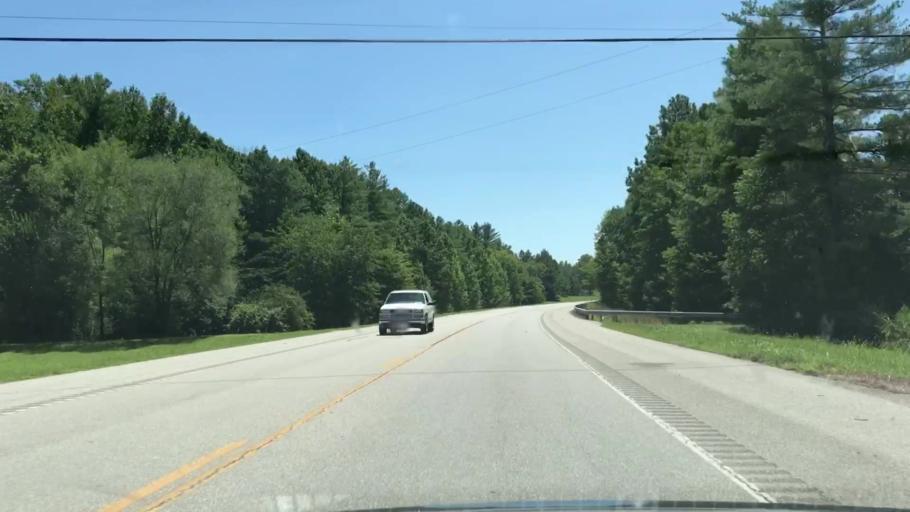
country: US
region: Tennessee
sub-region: Putnam County
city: Baxter
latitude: 36.2110
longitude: -85.6125
